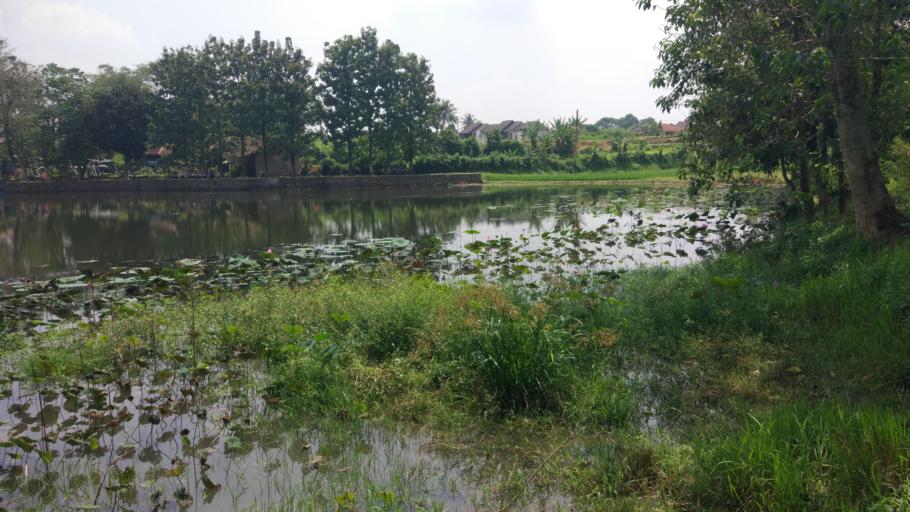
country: ID
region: West Java
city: Ciampea
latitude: -6.5460
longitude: 106.7329
